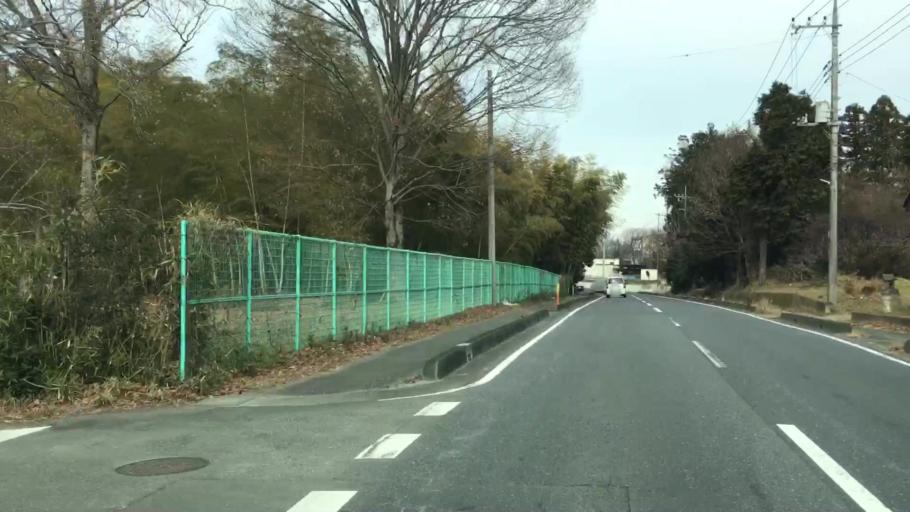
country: JP
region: Saitama
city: Kumagaya
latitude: 36.1206
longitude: 139.3264
